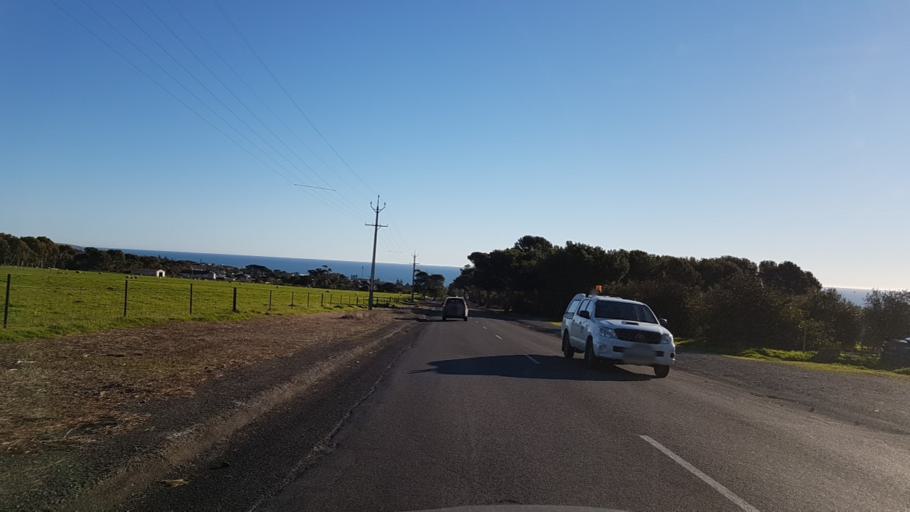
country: AU
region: South Australia
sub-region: Onkaparinga
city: Aldinga
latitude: -35.3291
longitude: 138.4672
